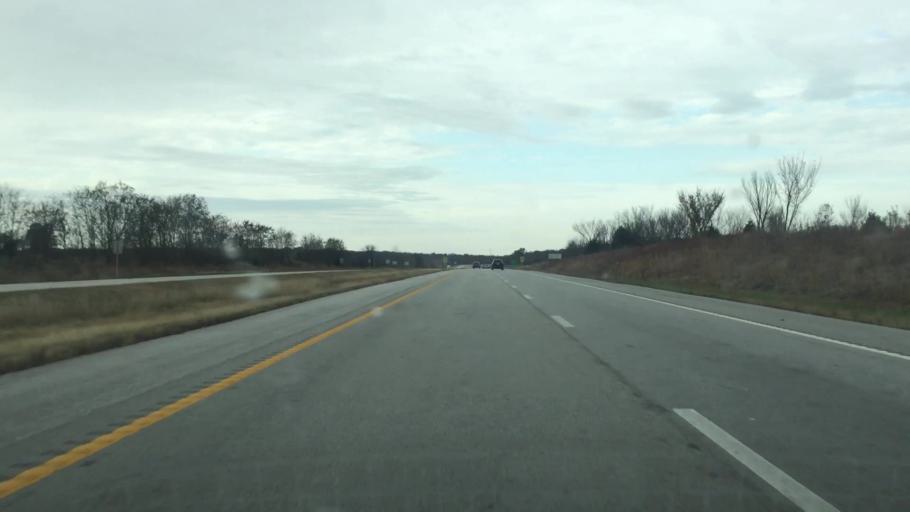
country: US
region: Missouri
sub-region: Saint Clair County
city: Osceola
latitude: 38.2027
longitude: -93.7501
